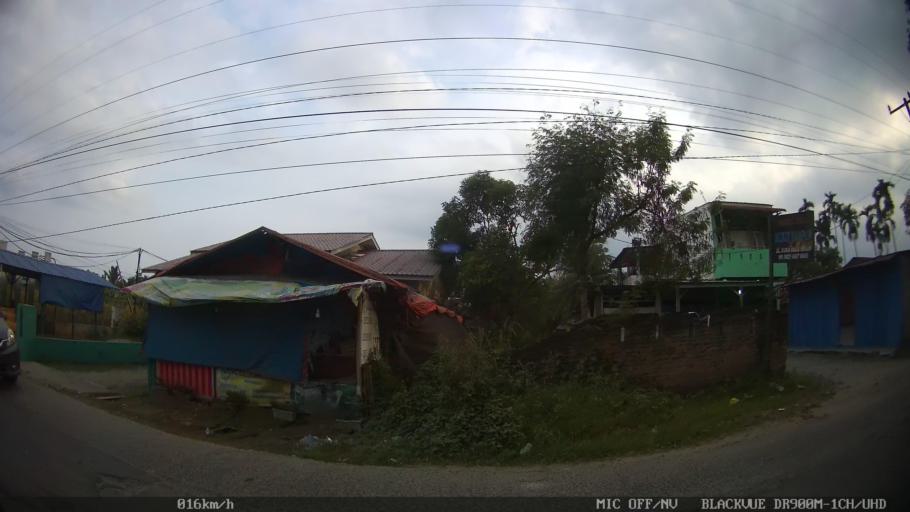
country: ID
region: North Sumatra
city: Sunggal
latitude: 3.5610
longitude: 98.5807
